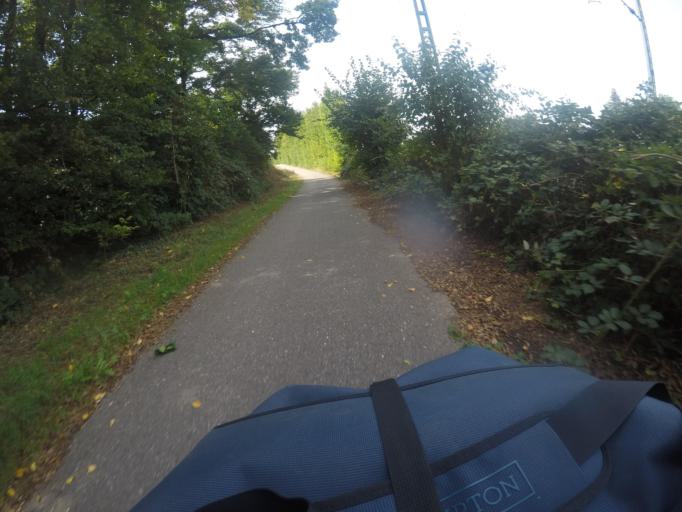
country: DE
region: Baden-Wuerttemberg
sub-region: Freiburg Region
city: Ebringen
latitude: 47.9720
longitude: 7.7840
